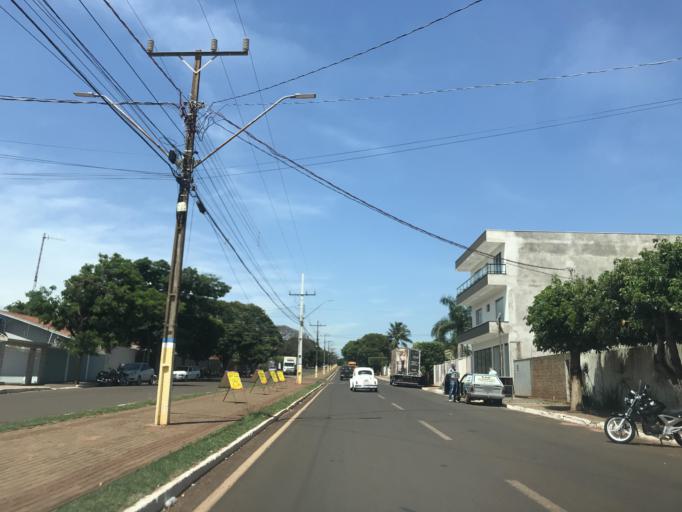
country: BR
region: Parana
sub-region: Paranavai
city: Nova Aurora
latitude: -22.9403
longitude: -52.6901
